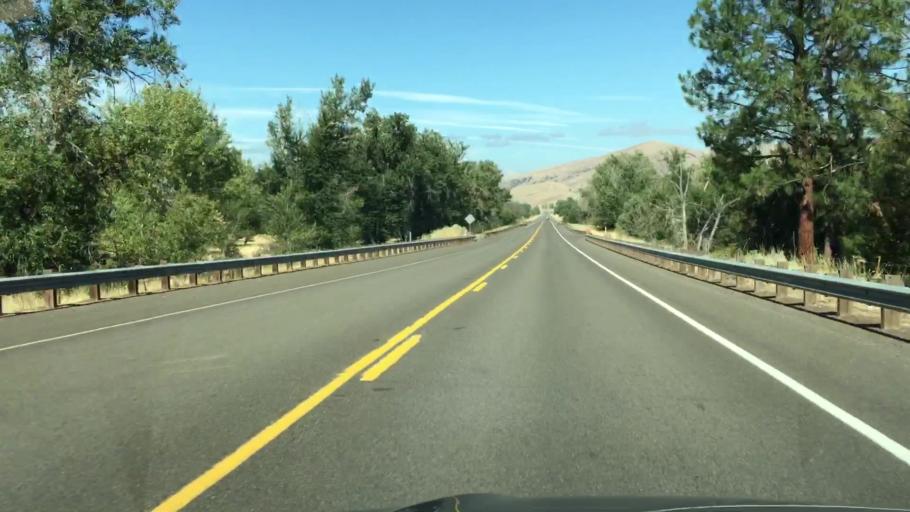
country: US
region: Oregon
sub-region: Wasco County
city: The Dalles
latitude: 45.2395
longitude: -121.1488
